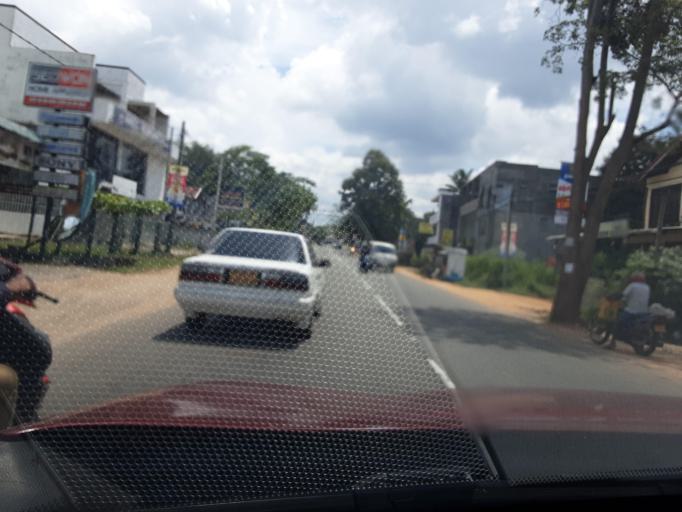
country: LK
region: North Western
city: Kurunegala
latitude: 7.4737
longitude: 80.3264
